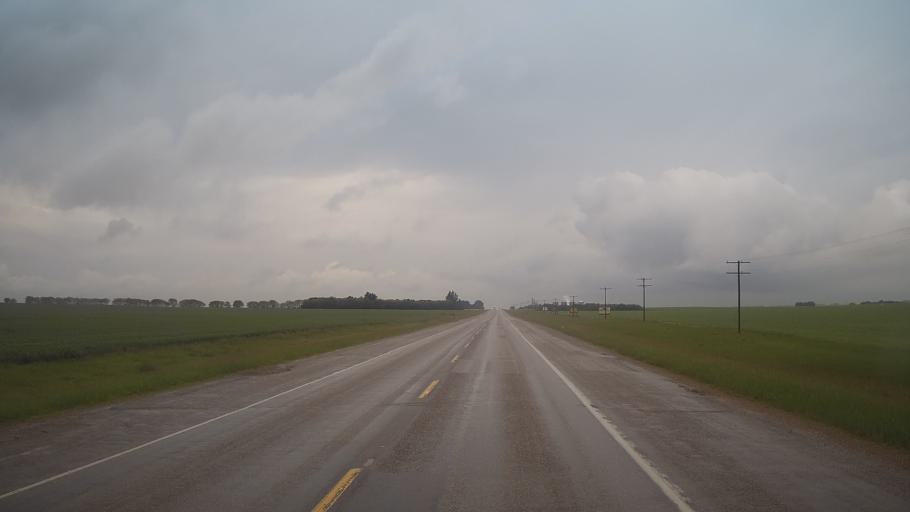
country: CA
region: Saskatchewan
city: Unity
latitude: 52.4350
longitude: -109.0746
